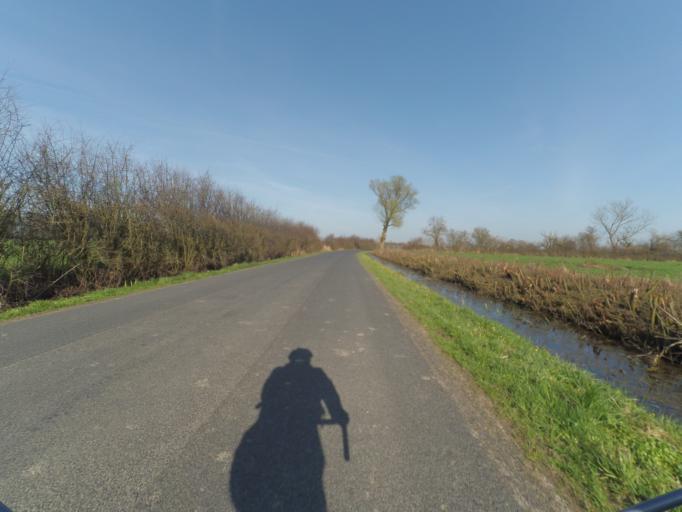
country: DE
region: North Rhine-Westphalia
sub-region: Regierungsbezirk Dusseldorf
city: Kranenburg
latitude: 51.8117
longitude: 6.0248
